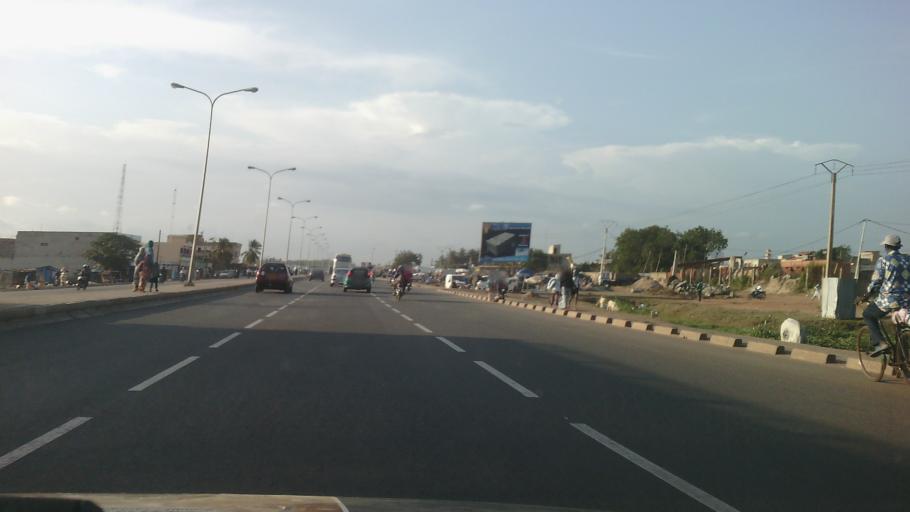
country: TG
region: Maritime
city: Lome
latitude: 6.2502
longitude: 1.2092
